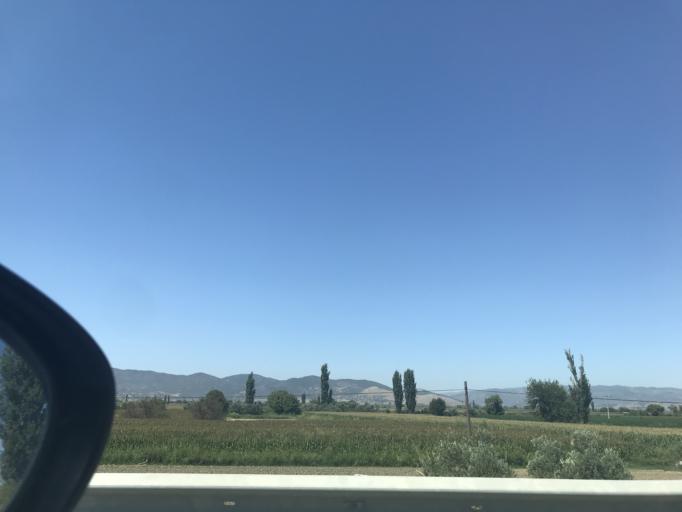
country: TR
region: Aydin
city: Cine
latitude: 37.5772
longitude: 28.0578
